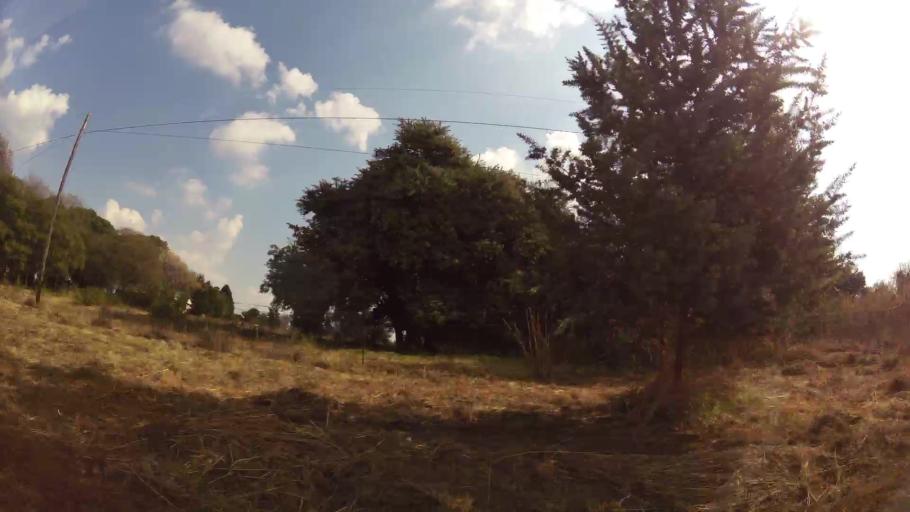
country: ZA
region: Mpumalanga
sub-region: Nkangala District Municipality
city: Delmas
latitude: -26.1641
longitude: 28.5480
